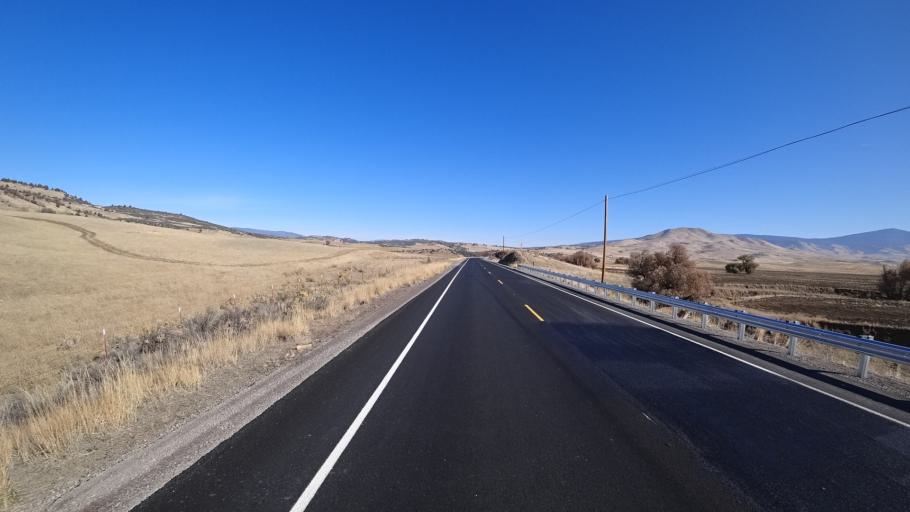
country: US
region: California
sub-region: Siskiyou County
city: Montague
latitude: 41.8385
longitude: -122.4813
